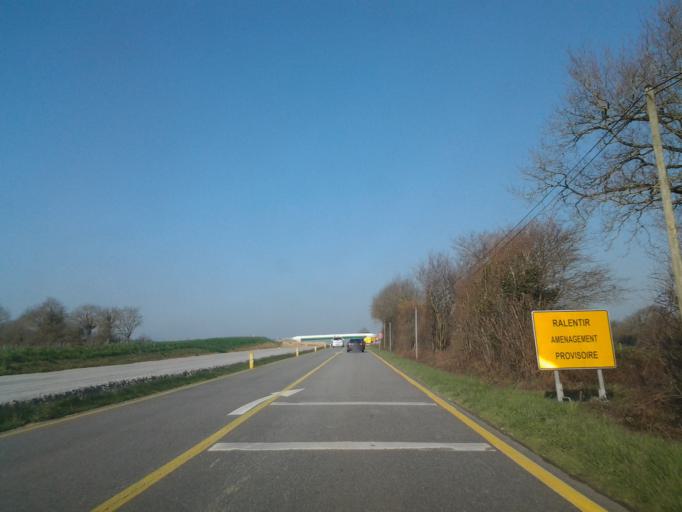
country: FR
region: Pays de la Loire
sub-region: Departement de la Vendee
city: Aizenay
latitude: 46.7555
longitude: -1.6381
